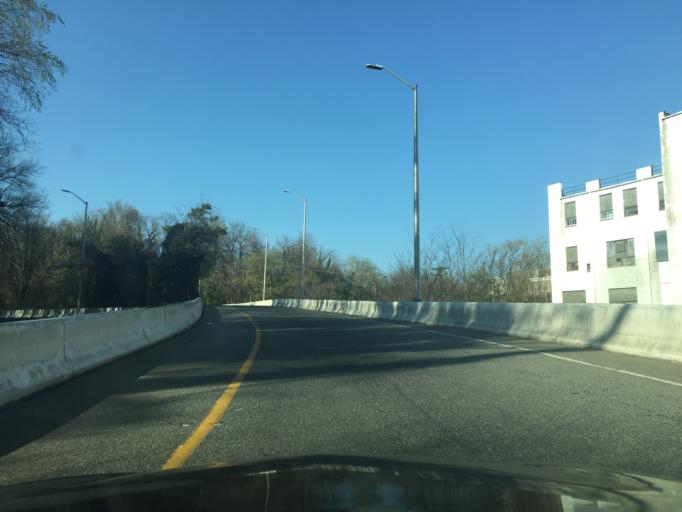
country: US
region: Maryland
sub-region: City of Baltimore
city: Baltimore
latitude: 39.3262
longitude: -76.6331
